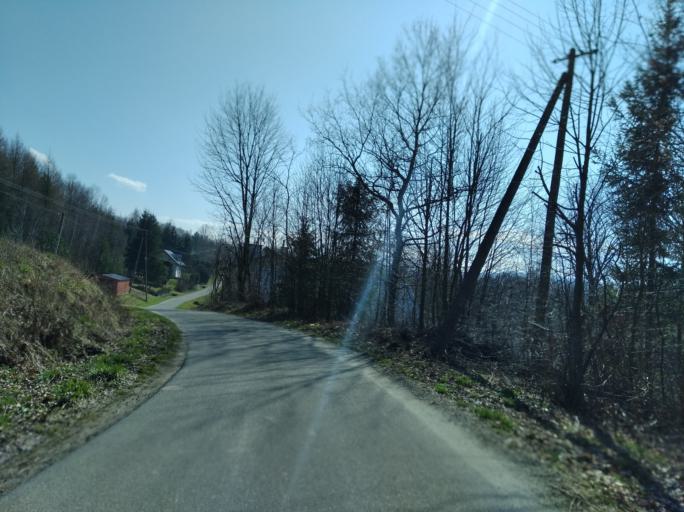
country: PL
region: Subcarpathian Voivodeship
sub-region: Powiat strzyzowski
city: Wysoka Strzyzowska
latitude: 49.8413
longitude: 21.7393
